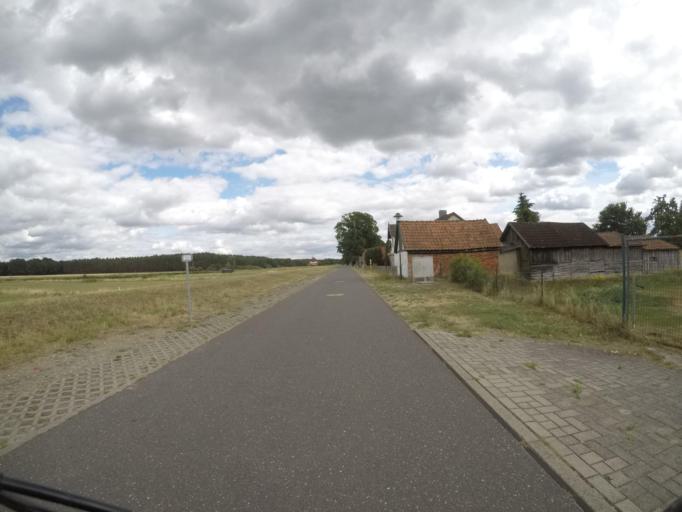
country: DE
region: Mecklenburg-Vorpommern
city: Lubtheen
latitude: 53.2990
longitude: 10.9729
